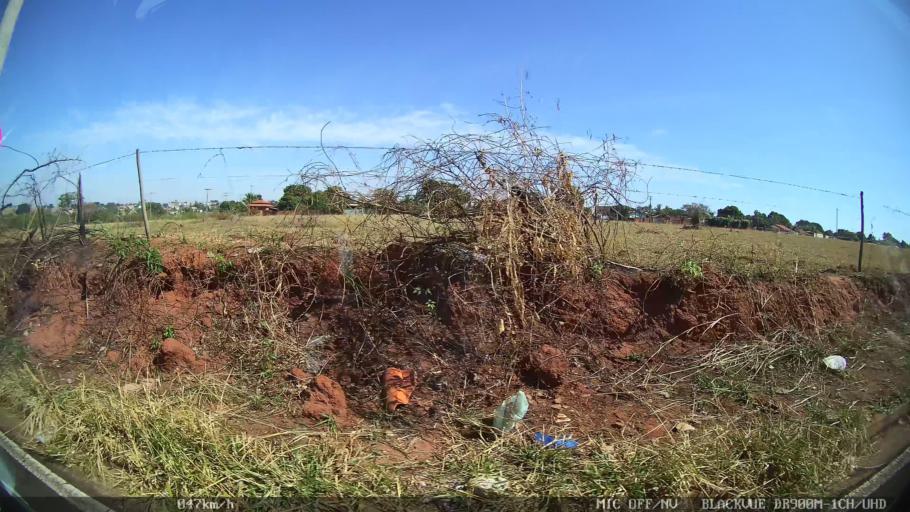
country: BR
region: Sao Paulo
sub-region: Sao Jose Do Rio Preto
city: Sao Jose do Rio Preto
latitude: -20.7586
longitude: -49.4238
